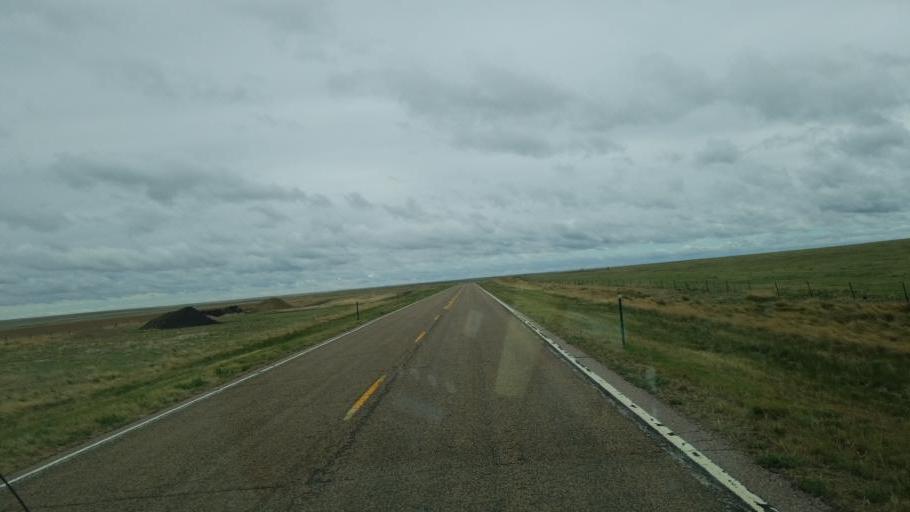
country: US
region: Colorado
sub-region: Lincoln County
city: Hugo
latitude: 38.8508
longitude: -103.4642
